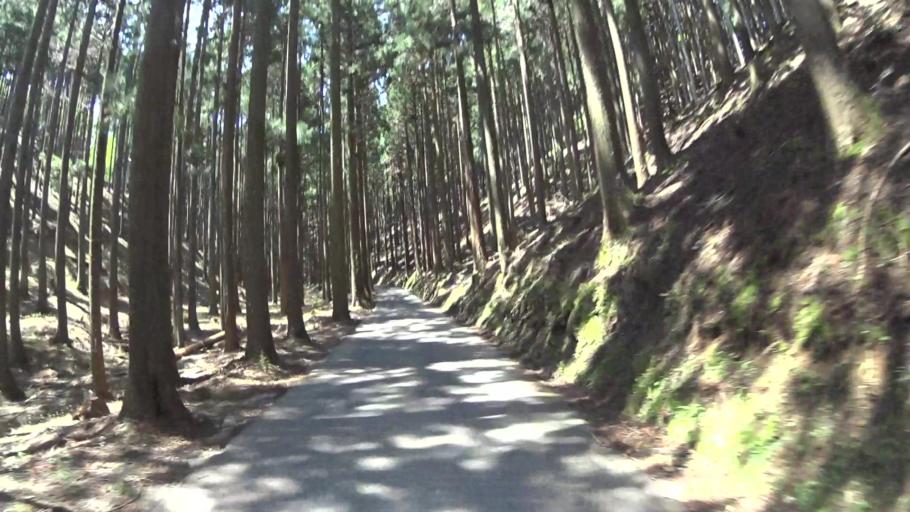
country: JP
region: Shiga Prefecture
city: Kitahama
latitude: 35.1568
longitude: 135.8003
